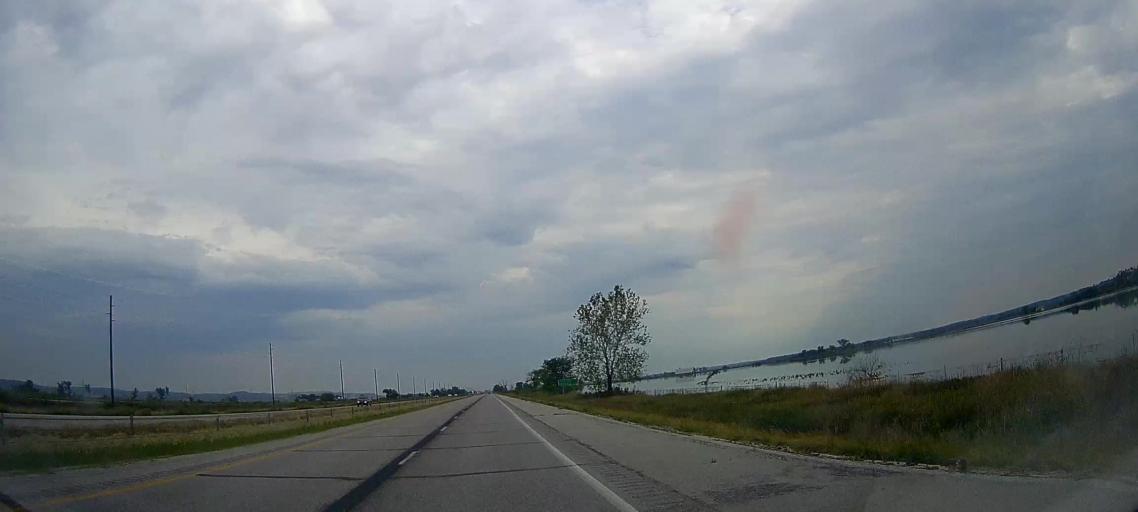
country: US
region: Iowa
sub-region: Pottawattamie County
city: Carter Lake
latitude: 41.4091
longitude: -95.8997
